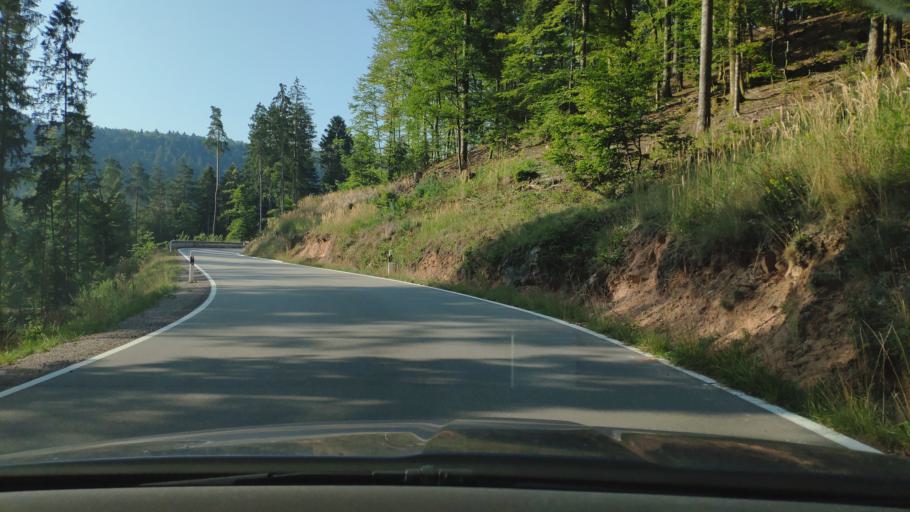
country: DE
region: Rheinland-Pfalz
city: Eppenbrunn
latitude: 49.1030
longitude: 7.6052
